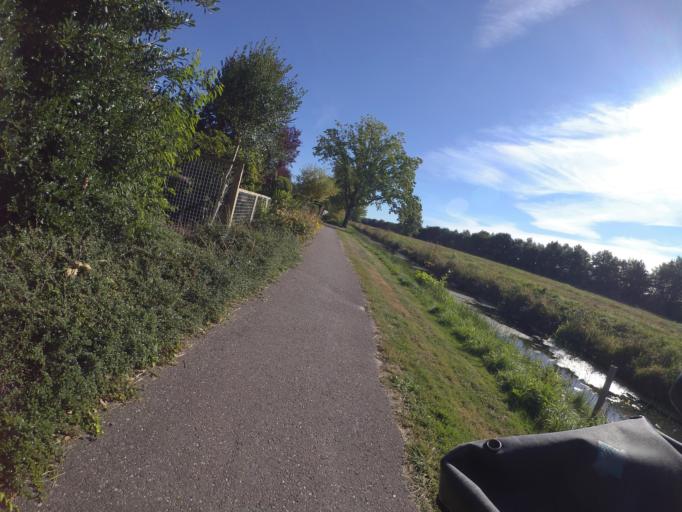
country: NL
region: Drenthe
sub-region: Gemeente Hoogeveen
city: Hoogeveen
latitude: 52.7135
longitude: 6.5007
